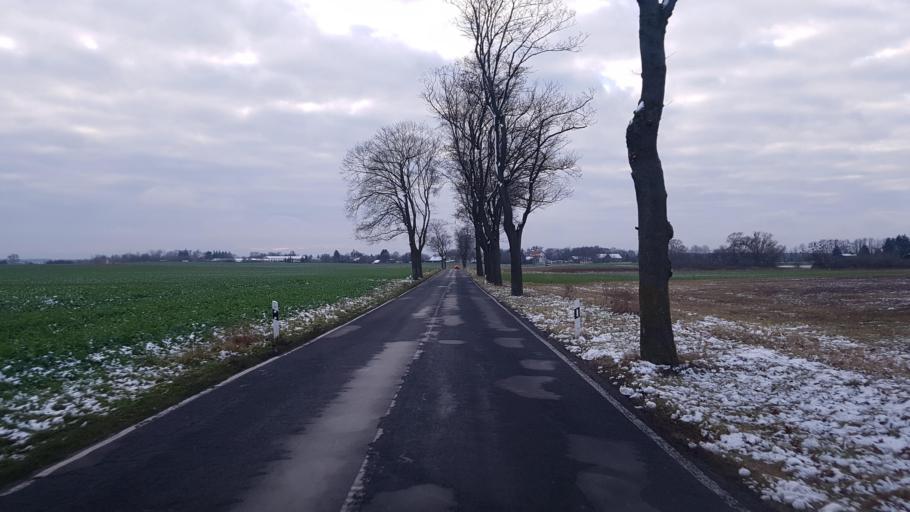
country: DE
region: Brandenburg
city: Rehfelde
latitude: 52.5203
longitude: 13.9068
